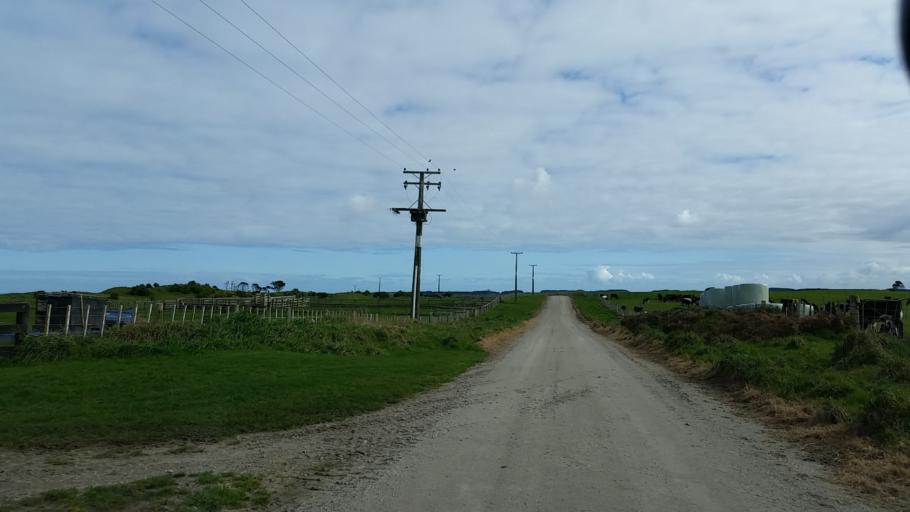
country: NZ
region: Taranaki
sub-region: South Taranaki District
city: Patea
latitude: -39.8070
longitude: 174.6603
